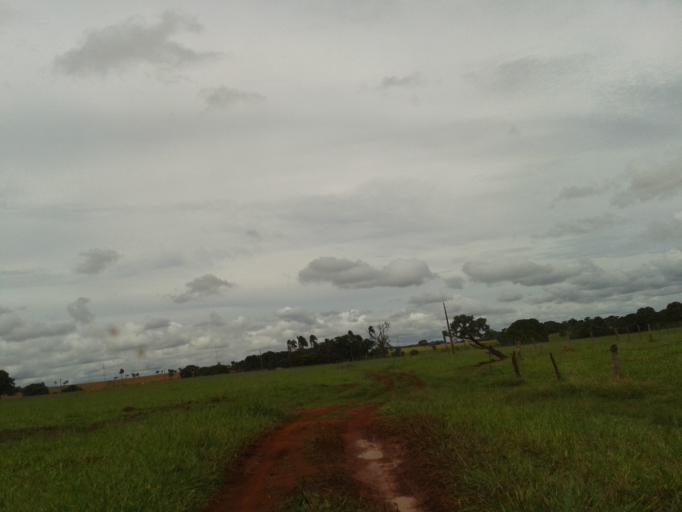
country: BR
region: Minas Gerais
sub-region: Capinopolis
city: Capinopolis
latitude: -18.7769
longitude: -49.7774
